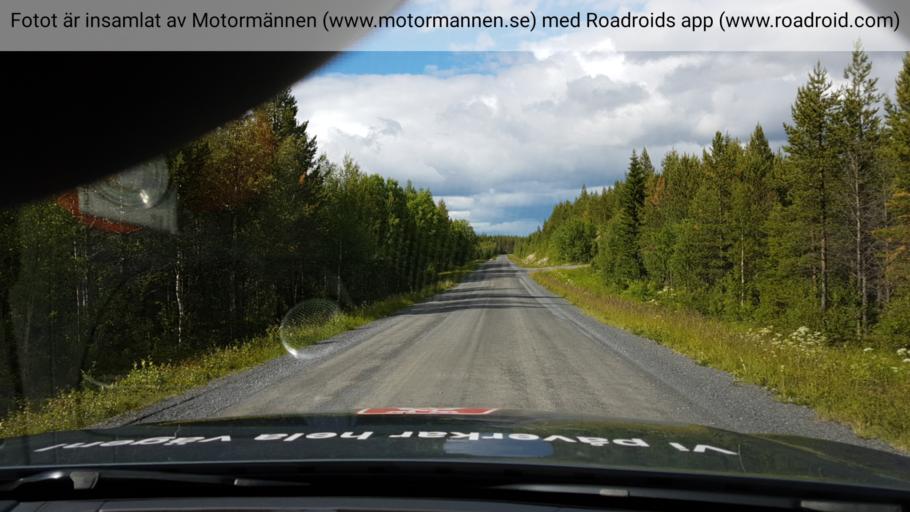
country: SE
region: Jaemtland
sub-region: Krokoms Kommun
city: Valla
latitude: 63.0664
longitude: 13.9590
